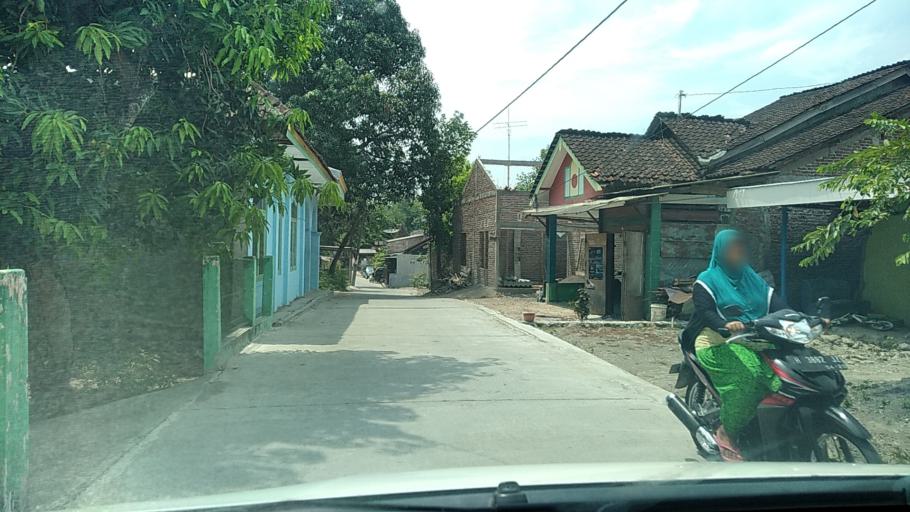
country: ID
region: Central Java
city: Mranggen
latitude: -7.0565
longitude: 110.4764
